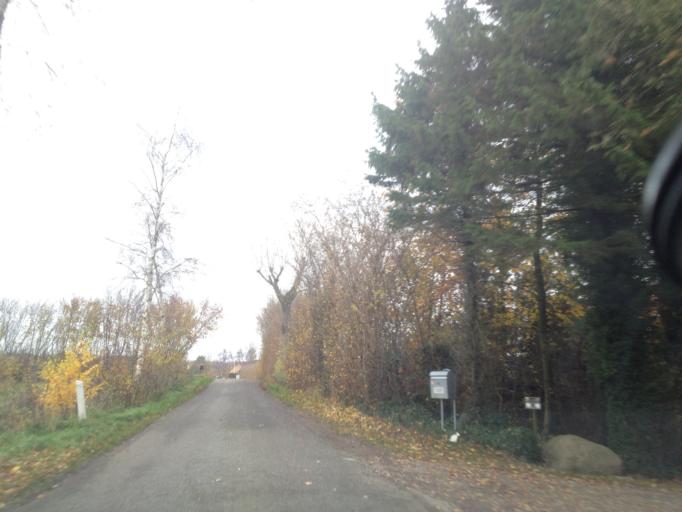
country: DK
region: South Denmark
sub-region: Assens Kommune
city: Vissenbjerg
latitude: 55.4119
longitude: 10.1535
